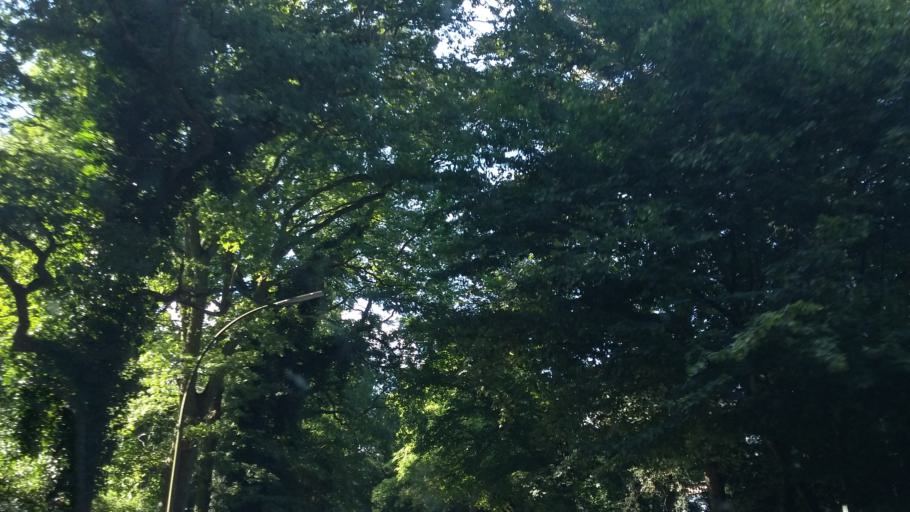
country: DE
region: Schleswig-Holstein
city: Halstenbek
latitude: 53.5537
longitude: 9.8388
